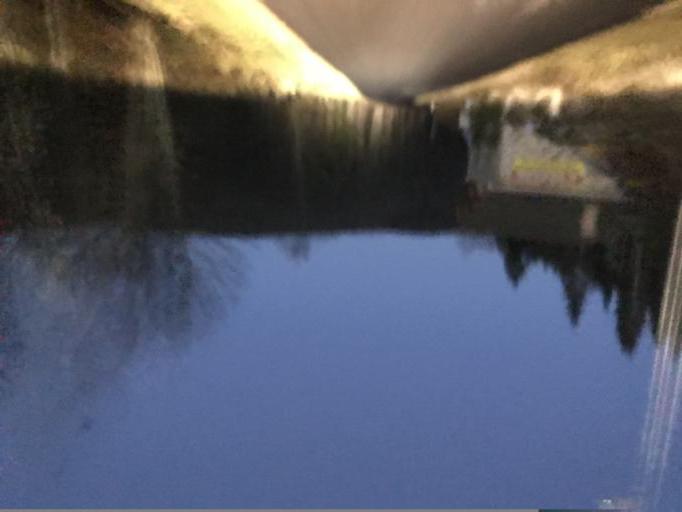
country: FR
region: Rhone-Alpes
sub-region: Departement de la Loire
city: Noiretable
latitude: 45.7339
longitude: 3.7335
